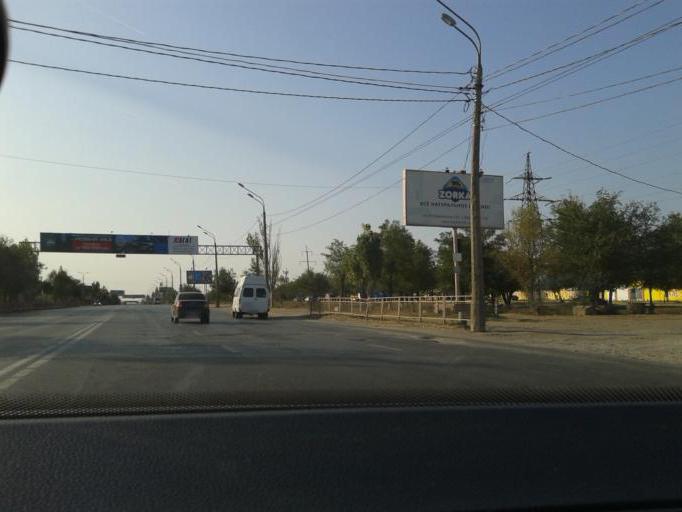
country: RU
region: Volgograd
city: Gorodishche
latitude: 48.7670
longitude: 44.4737
